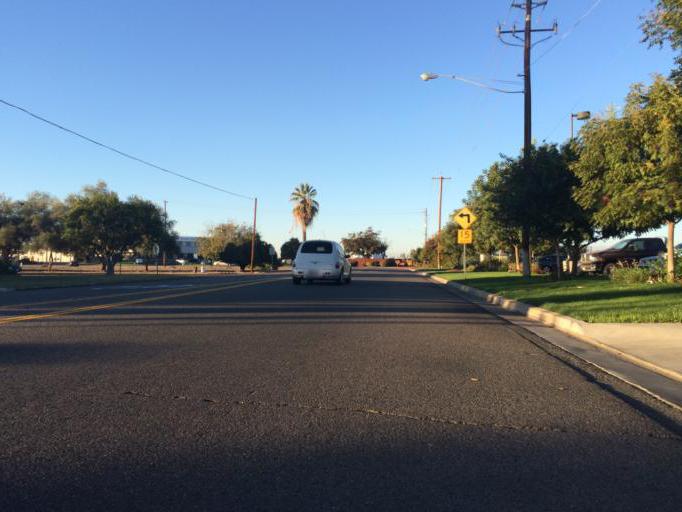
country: US
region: California
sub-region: Fresno County
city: Tarpey Village
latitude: 36.7783
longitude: -119.7317
